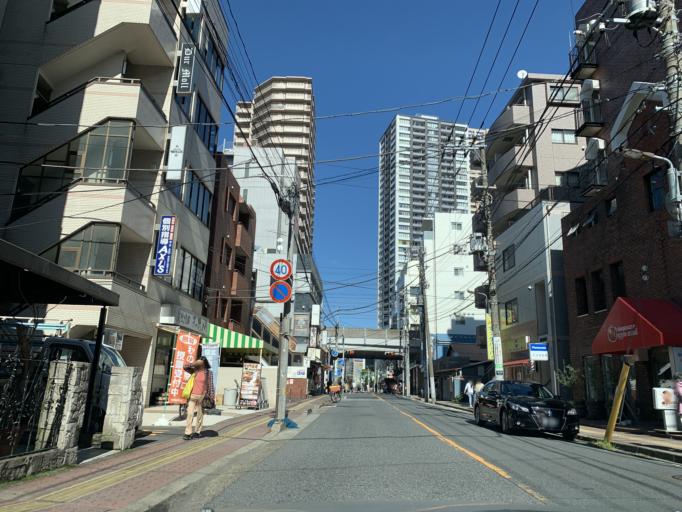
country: JP
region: Tokyo
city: Urayasu
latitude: 35.7209
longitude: 139.9253
